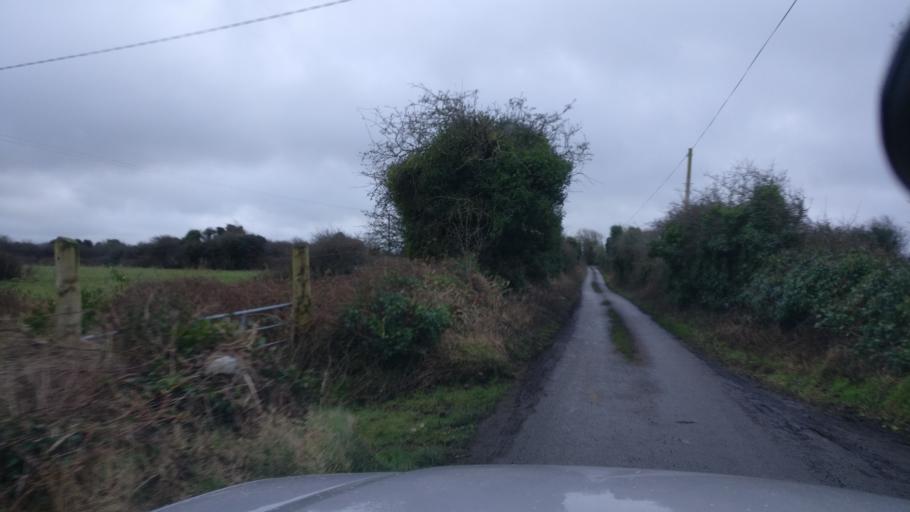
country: IE
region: Connaught
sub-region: County Galway
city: Athenry
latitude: 53.2076
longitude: -8.6783
